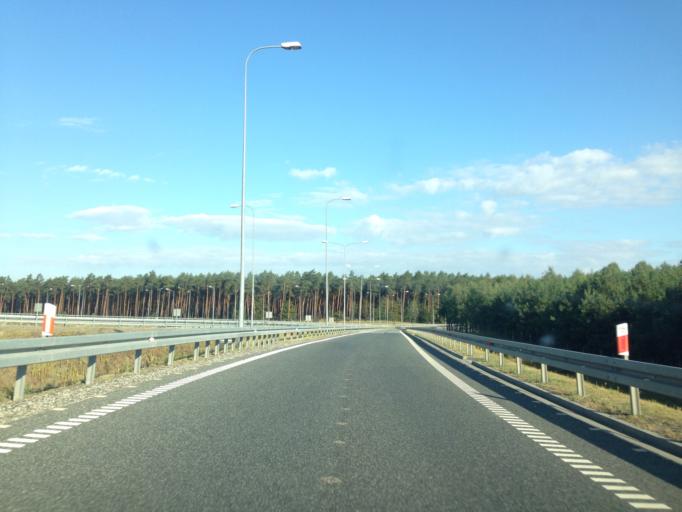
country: PL
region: Kujawsko-Pomorskie
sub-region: Bydgoszcz
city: Bydgoszcz
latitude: 53.0521
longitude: 18.0001
